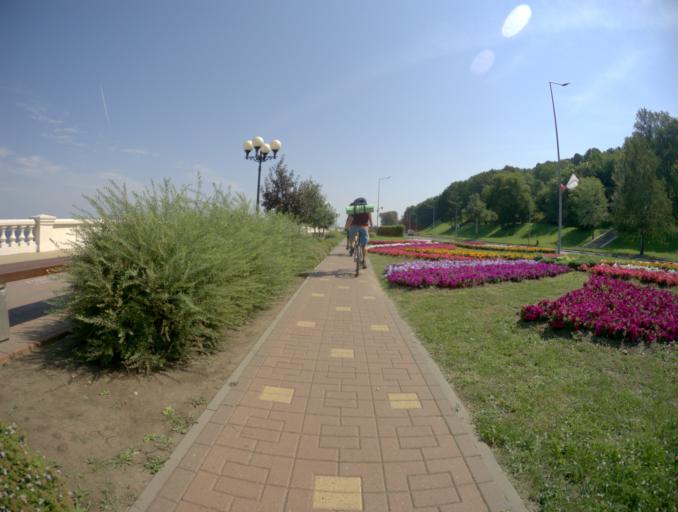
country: RU
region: Nizjnij Novgorod
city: Nizhniy Novgorod
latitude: 56.3320
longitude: 44.0131
